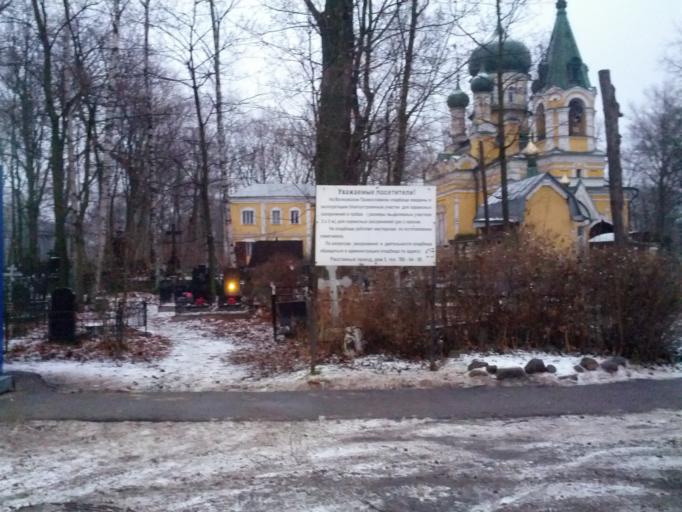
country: RU
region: St.-Petersburg
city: Centralniy
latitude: 59.9011
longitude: 30.3538
